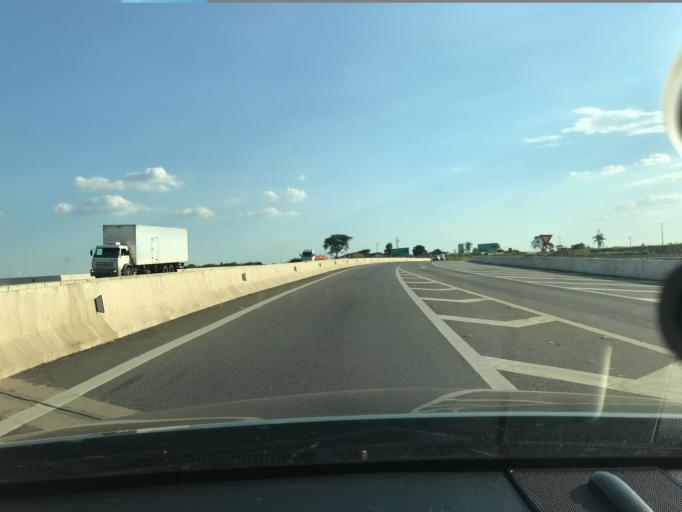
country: BR
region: Sao Paulo
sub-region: Valinhos
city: Valinhos
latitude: -23.0138
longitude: -47.0843
